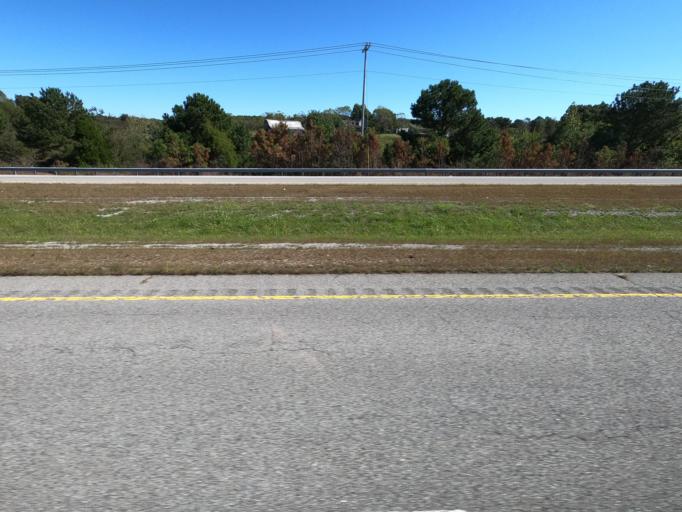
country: US
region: Tennessee
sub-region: Maury County
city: Mount Pleasant
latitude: 35.4589
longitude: -87.2689
